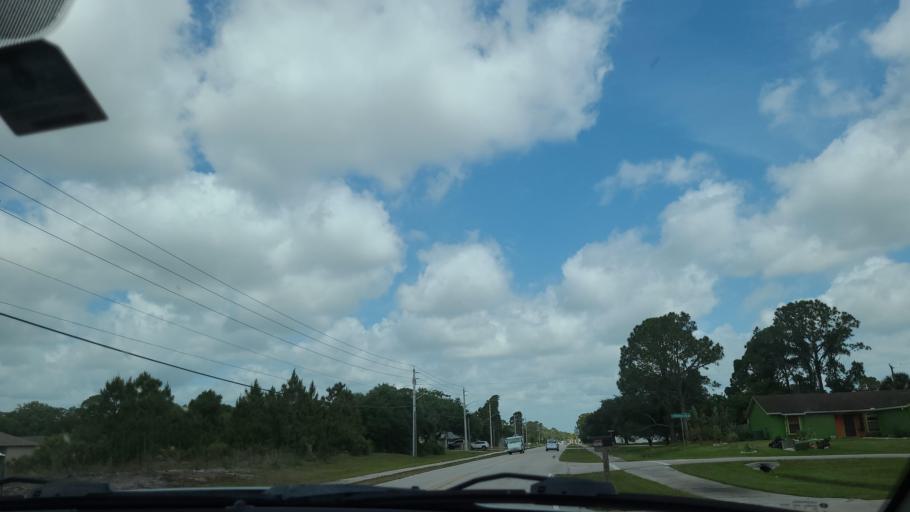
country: US
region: Florida
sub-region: Brevard County
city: June Park
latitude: 27.9883
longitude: -80.6916
